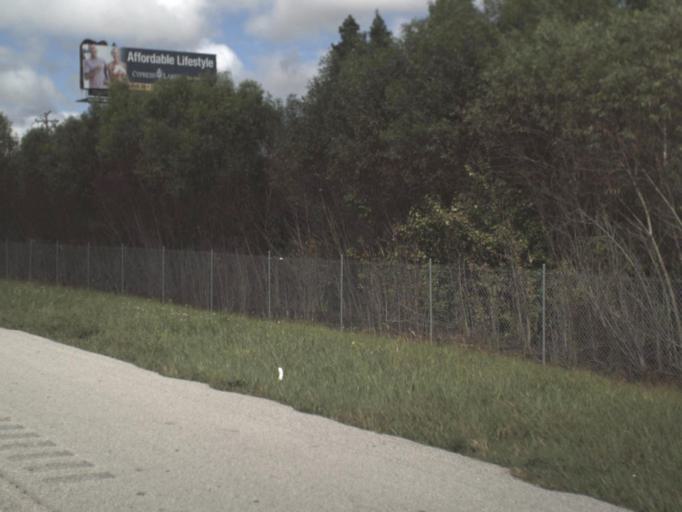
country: US
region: Florida
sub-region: Polk County
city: Gibsonia
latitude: 28.0944
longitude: -81.9568
